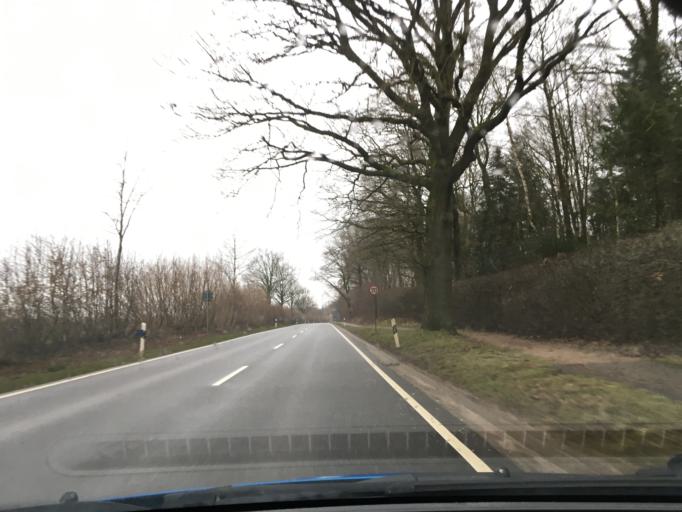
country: DE
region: Schleswig-Holstein
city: Hornbek
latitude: 53.5682
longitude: 10.6421
